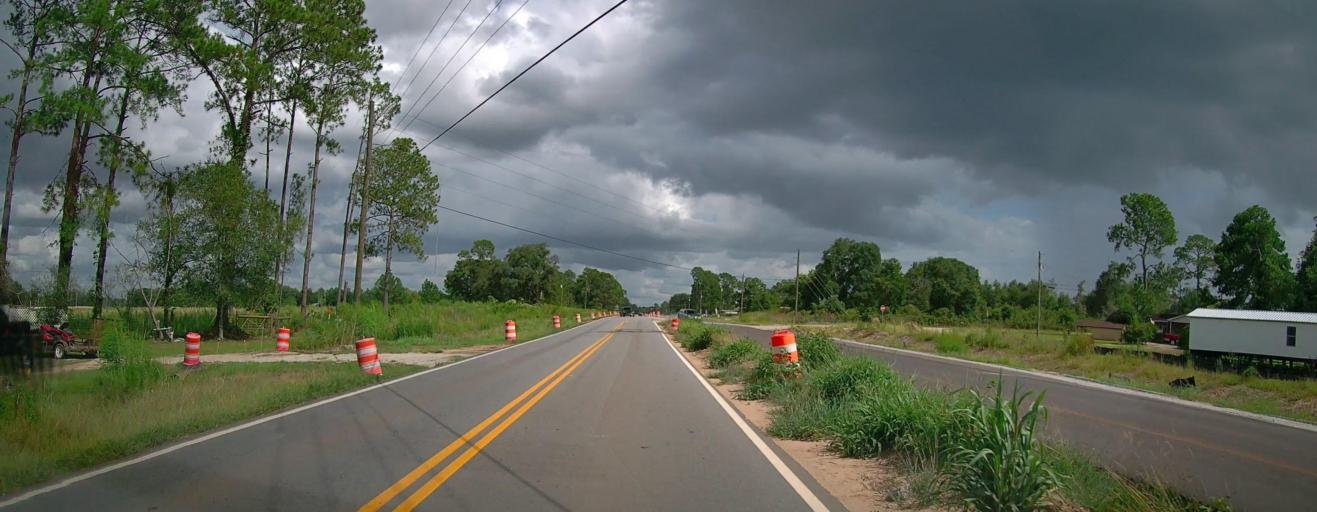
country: US
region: Georgia
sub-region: Coffee County
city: Douglas
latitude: 31.5333
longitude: -82.9152
